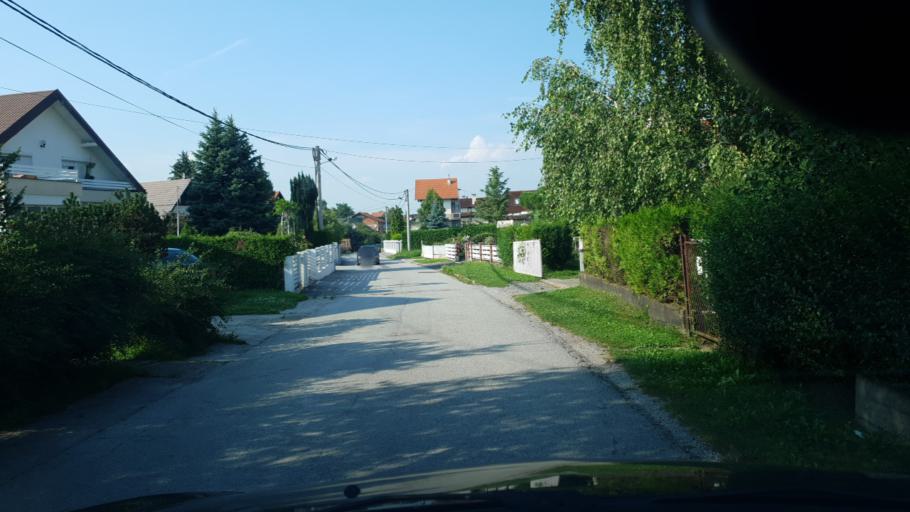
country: HR
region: Krapinsko-Zagorska
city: Oroslavje
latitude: 45.9748
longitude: 15.9209
